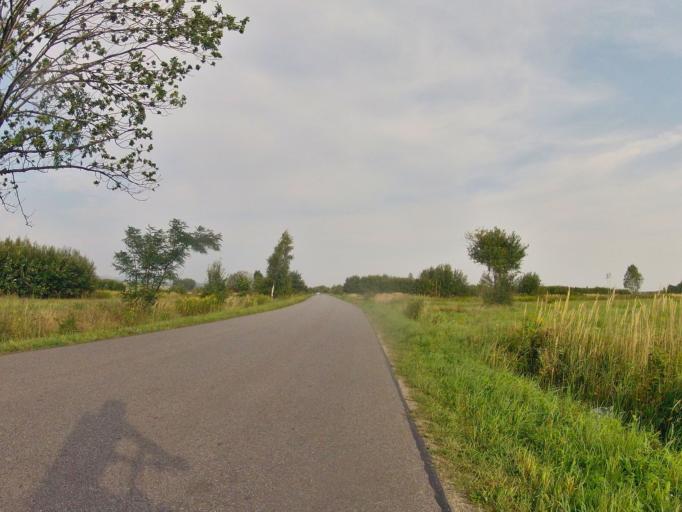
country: PL
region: Subcarpathian Voivodeship
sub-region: Powiat jasielski
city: Nowy Zmigrod
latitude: 49.6231
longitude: 21.5132
